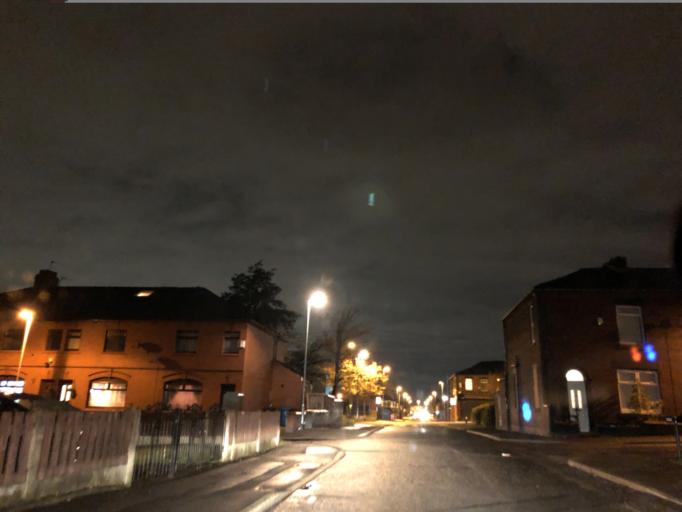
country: GB
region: England
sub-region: Borough of Oldham
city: Oldham
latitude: 53.5283
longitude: -2.1105
